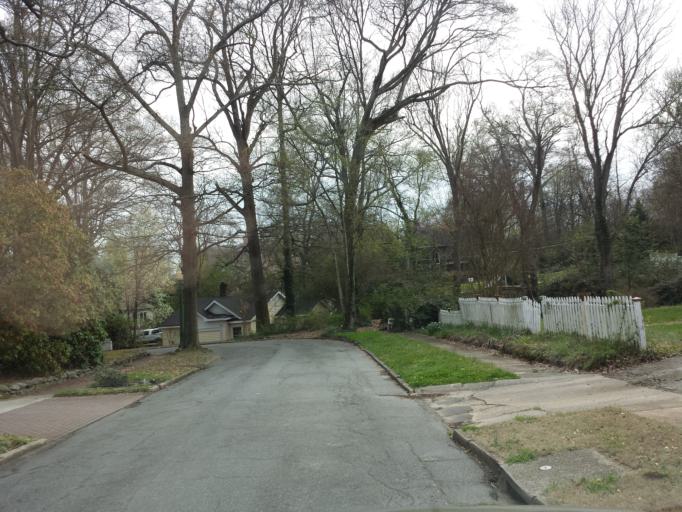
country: US
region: Georgia
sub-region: Cobb County
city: Marietta
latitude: 33.9582
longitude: -84.5465
